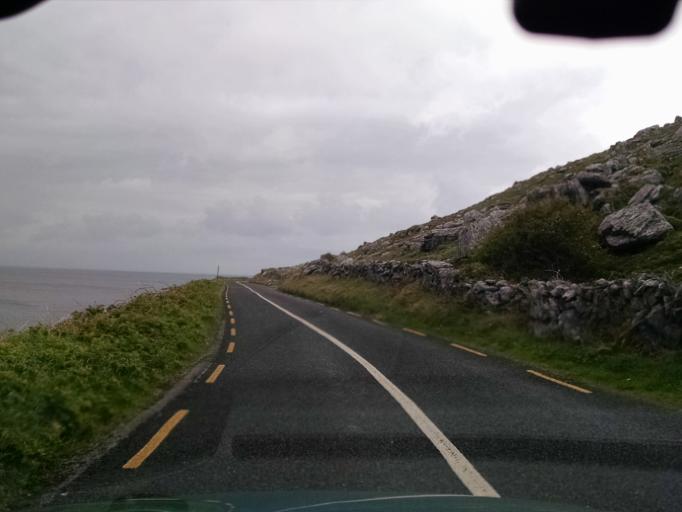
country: IE
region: Connaught
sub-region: County Galway
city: Bearna
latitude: 53.1498
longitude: -9.2486
